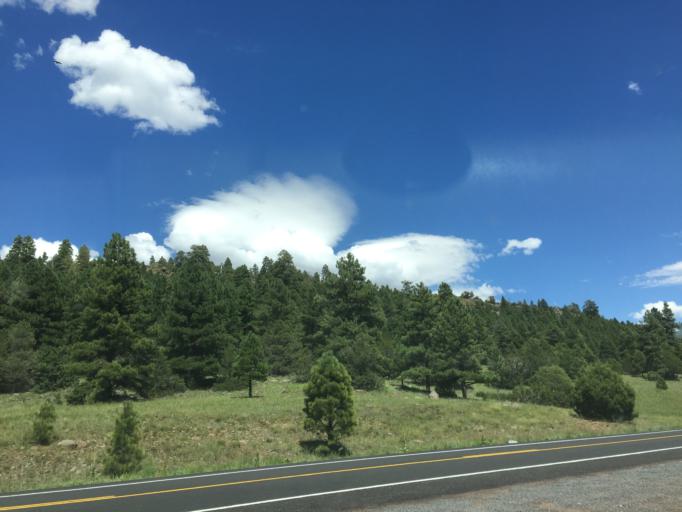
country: US
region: Arizona
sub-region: Coconino County
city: Mountainaire
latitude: 35.0606
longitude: -111.4807
